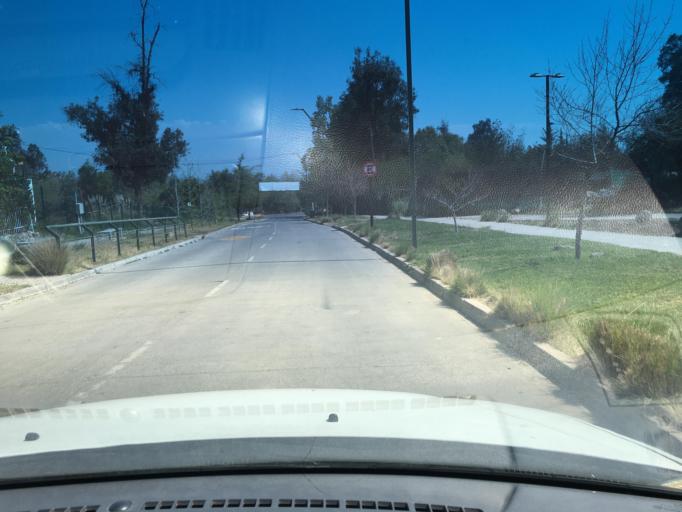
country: CL
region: Santiago Metropolitan
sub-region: Provincia de Santiago
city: Villa Presidente Frei, Nunoa, Santiago, Chile
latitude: -33.5125
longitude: -70.5367
